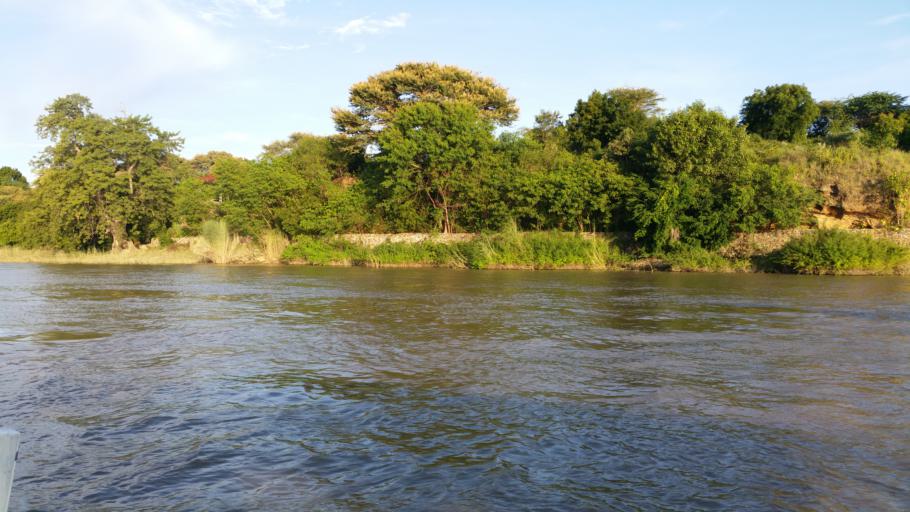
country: MM
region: Magway
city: Pakokku
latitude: 21.1871
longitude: 94.8792
